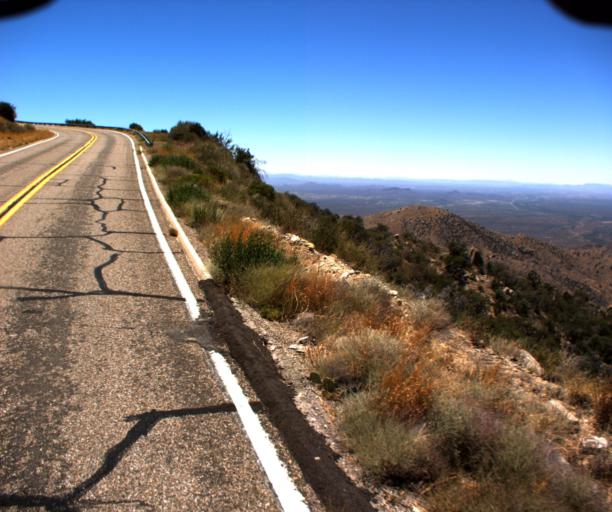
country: US
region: Arizona
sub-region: Pima County
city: Sells
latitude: 31.9566
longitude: -111.6262
